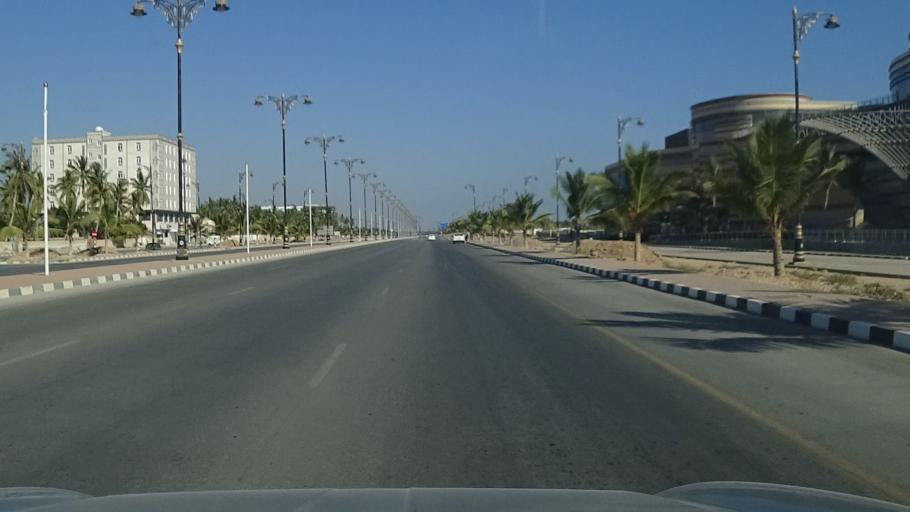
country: OM
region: Zufar
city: Salalah
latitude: 17.0359
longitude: 54.1635
